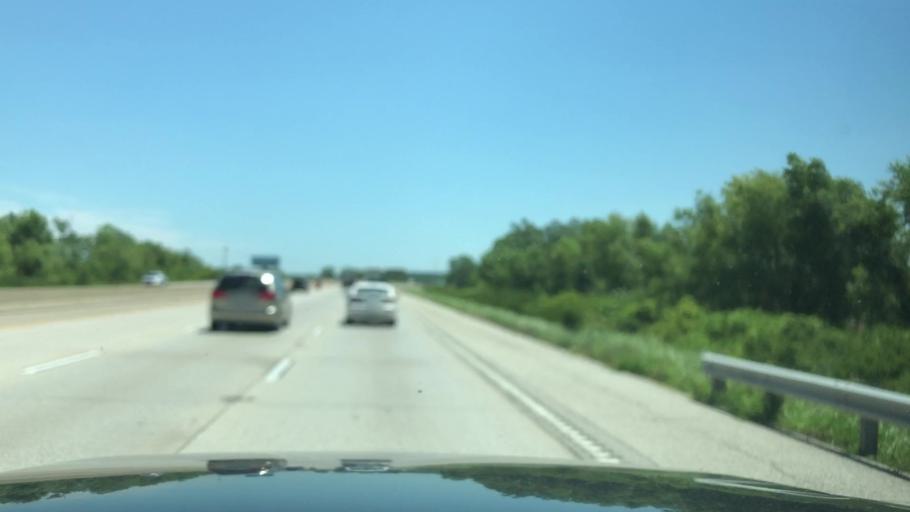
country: US
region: Missouri
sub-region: Saint Louis County
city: Bridgeton
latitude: 38.7900
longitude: -90.4290
